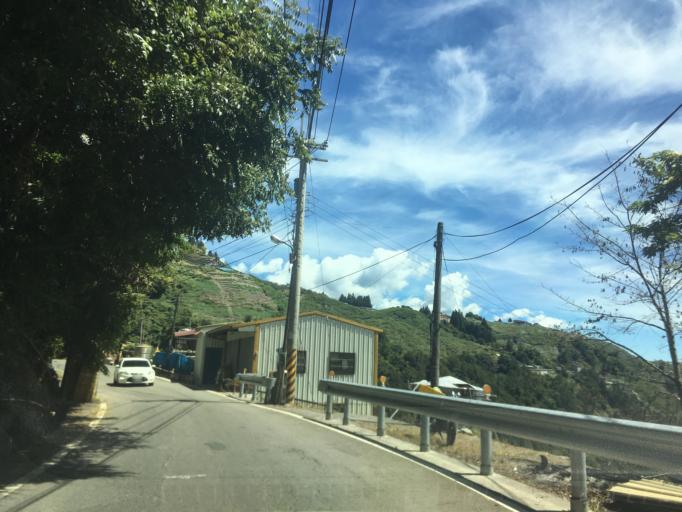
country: TW
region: Taiwan
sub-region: Nantou
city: Puli
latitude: 24.2446
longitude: 121.2554
